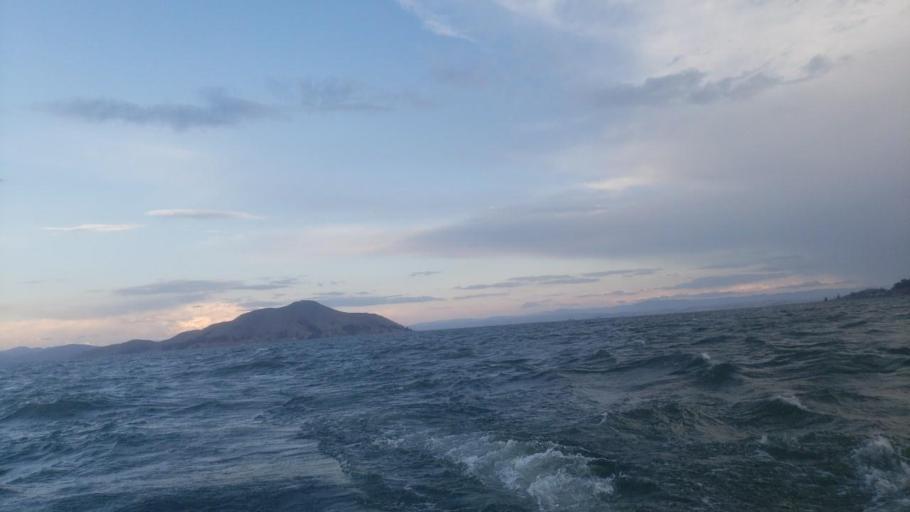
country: BO
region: La Paz
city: San Pedro
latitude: -16.2644
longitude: -68.8024
